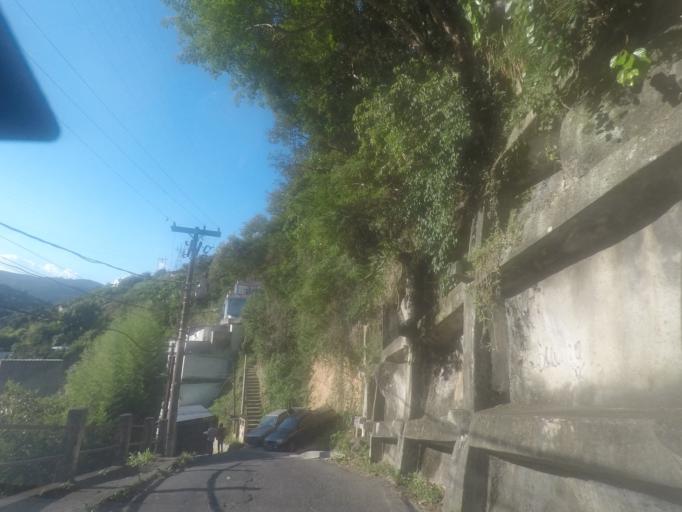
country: BR
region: Rio de Janeiro
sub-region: Petropolis
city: Petropolis
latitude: -22.4982
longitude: -43.1468
